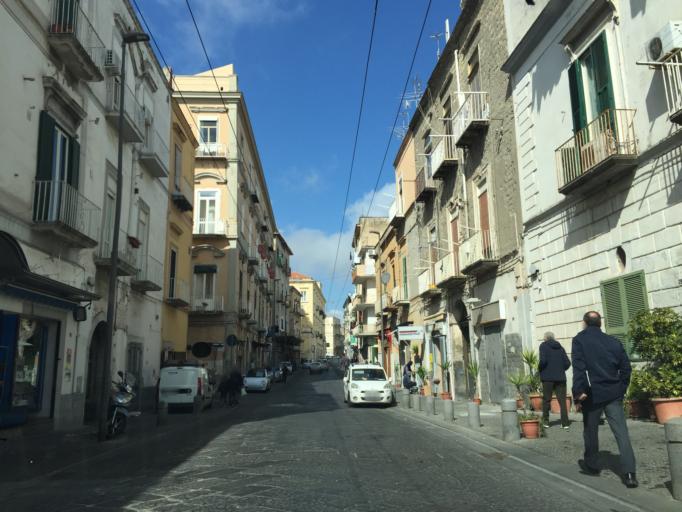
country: IT
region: Campania
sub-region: Provincia di Napoli
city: Ercolano
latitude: 40.8042
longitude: 14.3509
